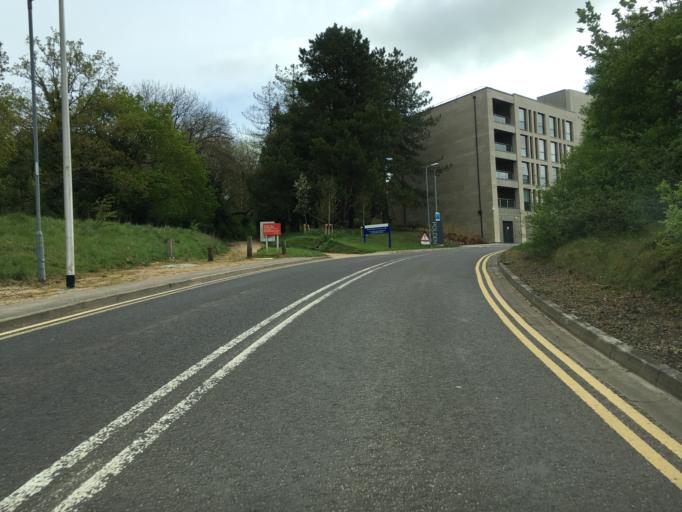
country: GB
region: England
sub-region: Bath and North East Somerset
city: Bath
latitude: 51.3803
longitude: -2.3339
